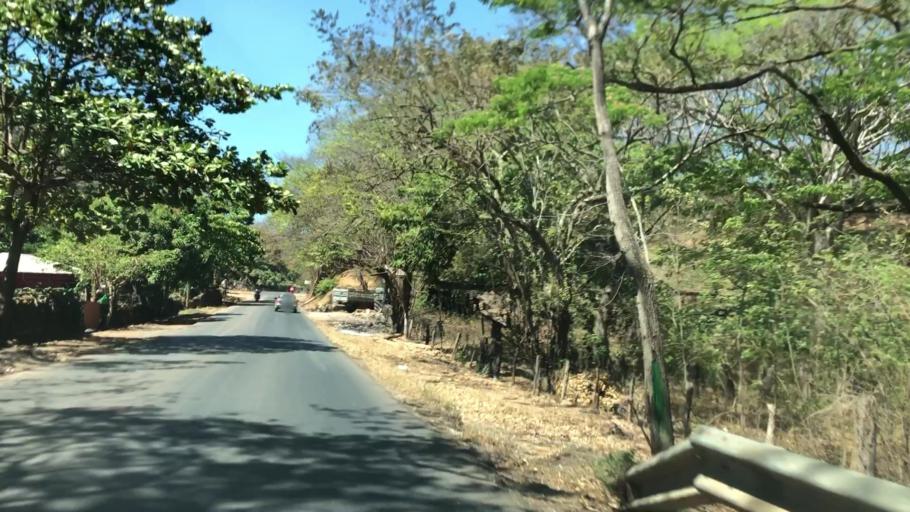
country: CR
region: Guanacaste
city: Belen
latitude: 10.3661
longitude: -85.7917
